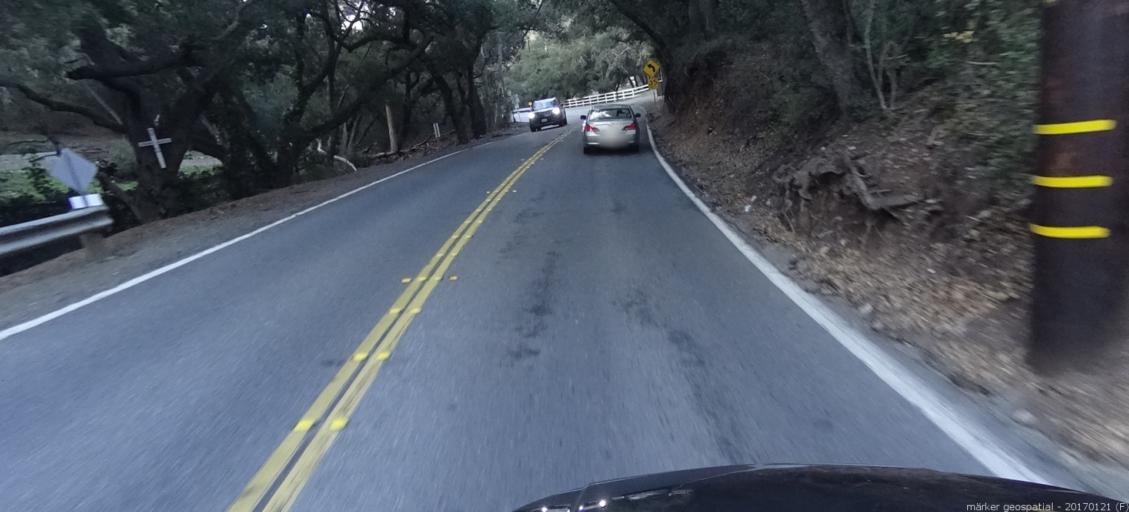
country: US
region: California
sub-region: Orange County
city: Trabuco Canyon
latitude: 33.6811
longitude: -117.6031
